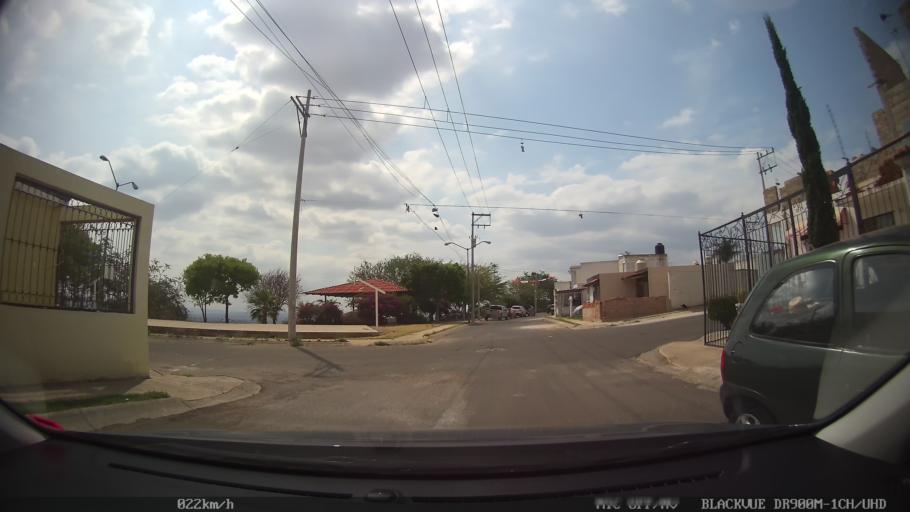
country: MX
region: Jalisco
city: Coyula
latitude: 20.6406
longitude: -103.2170
